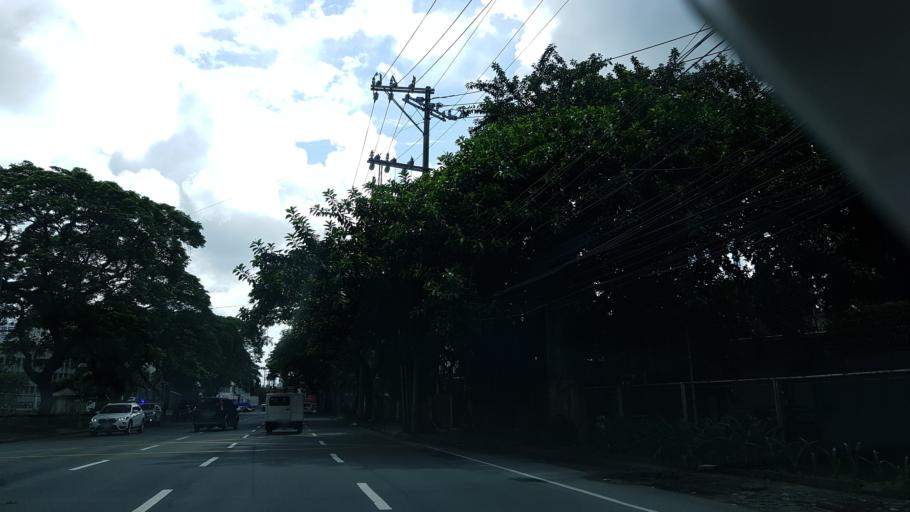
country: PH
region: Metro Manila
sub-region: Makati City
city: Makati City
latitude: 14.5591
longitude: 121.0289
